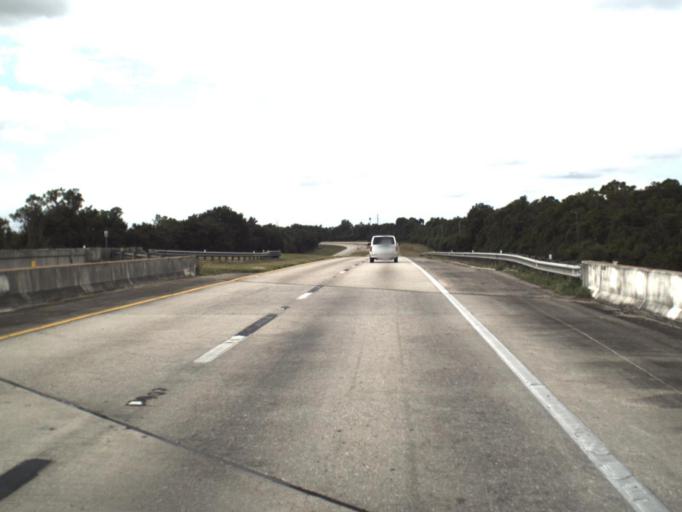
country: US
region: Florida
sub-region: Hardee County
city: Bowling Green
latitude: 27.6832
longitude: -81.8158
